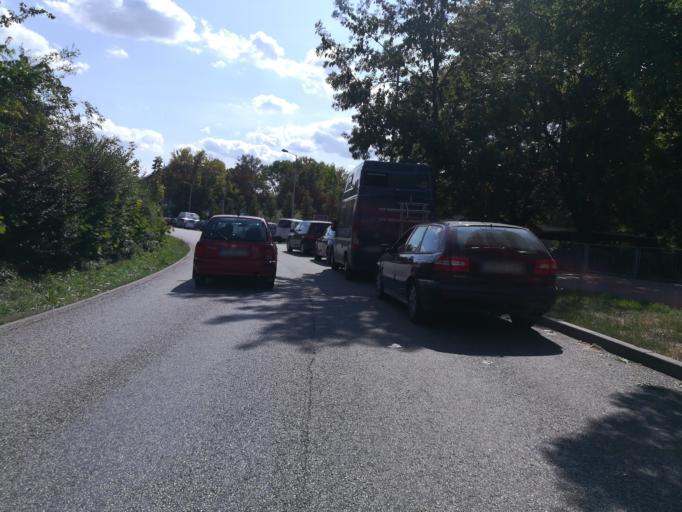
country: DE
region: Saxony-Anhalt
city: Magdeburg
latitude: 52.1387
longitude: 11.6089
